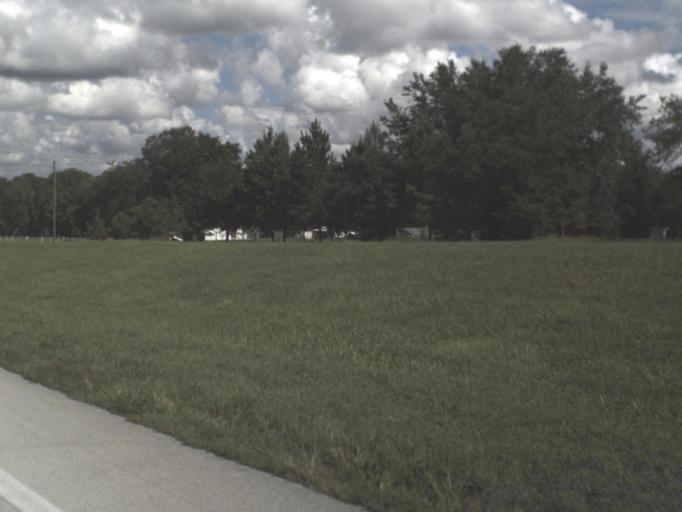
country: US
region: Florida
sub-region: Polk County
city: Polk City
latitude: 28.2955
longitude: -81.8348
